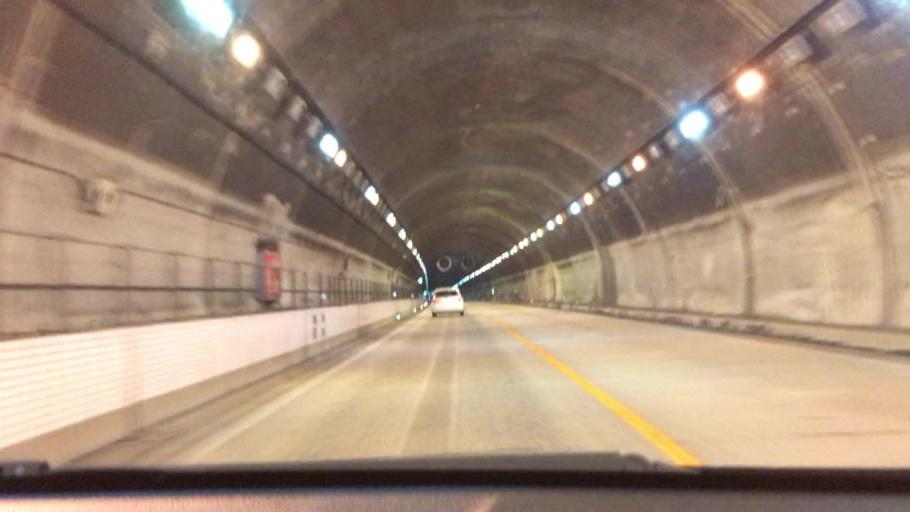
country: JP
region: Yamaguchi
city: Tokuyama
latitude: 34.0896
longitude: 131.7530
